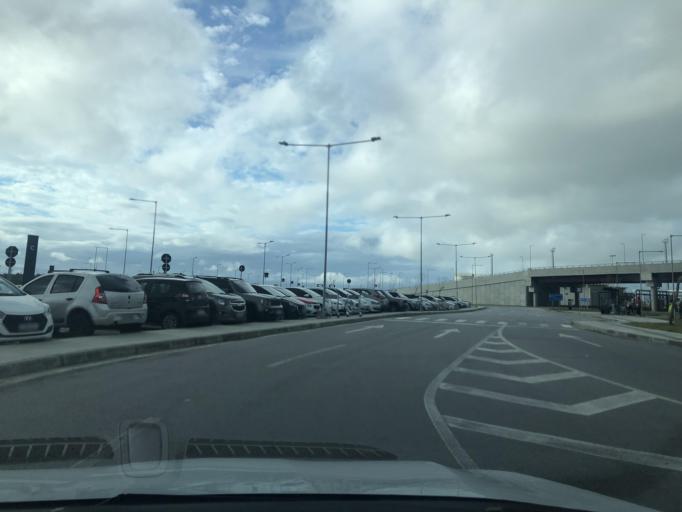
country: BR
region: Santa Catarina
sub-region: Florianopolis
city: Tapera
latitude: -27.6745
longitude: -48.5470
